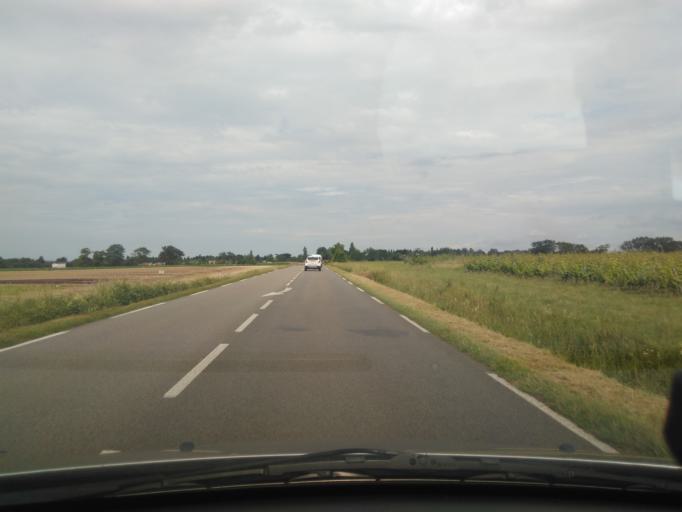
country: FR
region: Pays de la Loire
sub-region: Departement de la Loire-Atlantique
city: Bourgneuf-en-Retz
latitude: 47.0339
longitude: -1.9297
